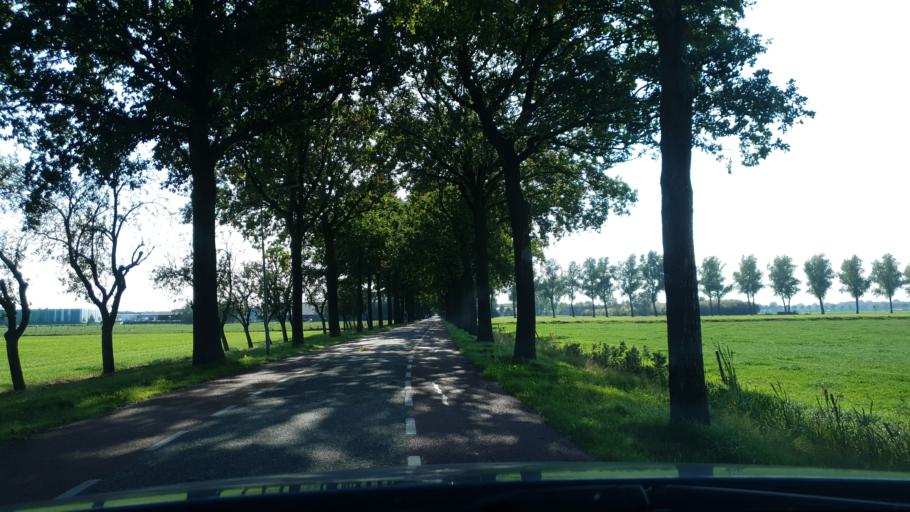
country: NL
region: Gelderland
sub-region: Gemeente Beuningen
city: Beuningen
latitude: 51.8400
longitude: 5.7506
